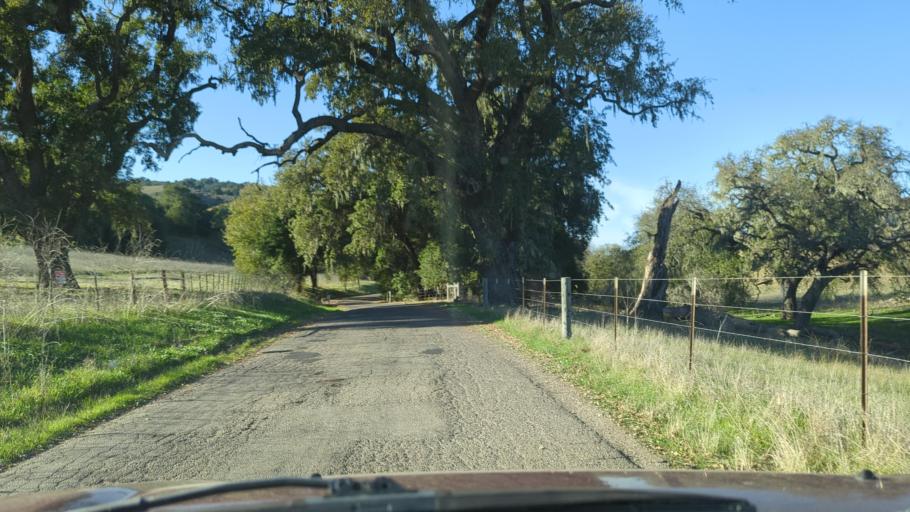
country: US
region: California
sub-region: Santa Barbara County
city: Santa Ynez
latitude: 34.5641
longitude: -120.0917
